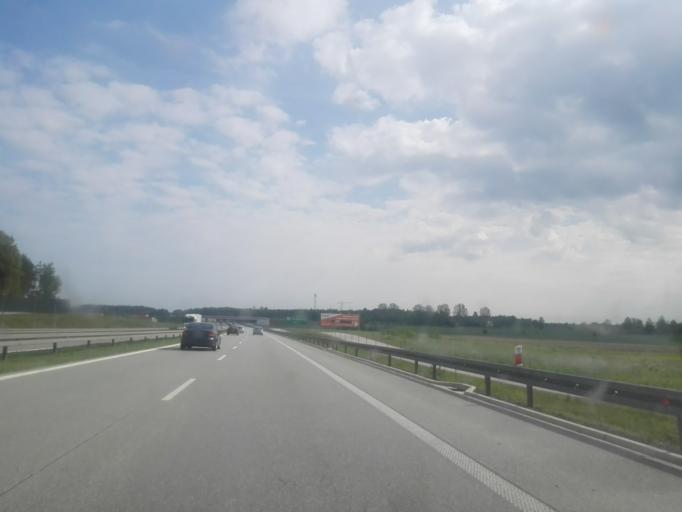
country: PL
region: Lodz Voivodeship
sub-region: Powiat tomaszowski
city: Czerniewice
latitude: 51.6898
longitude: 20.2072
